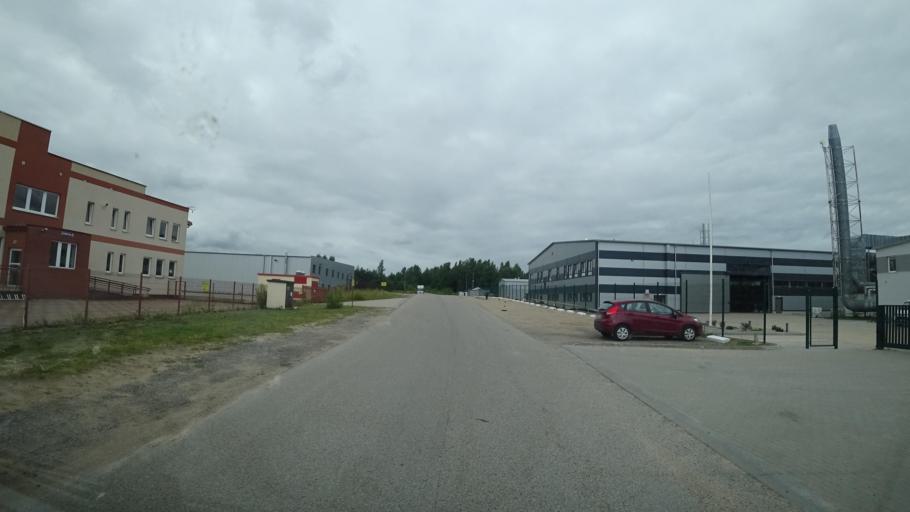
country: PL
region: Warmian-Masurian Voivodeship
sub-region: Powiat goldapski
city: Goldap
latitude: 54.3339
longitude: 22.2922
